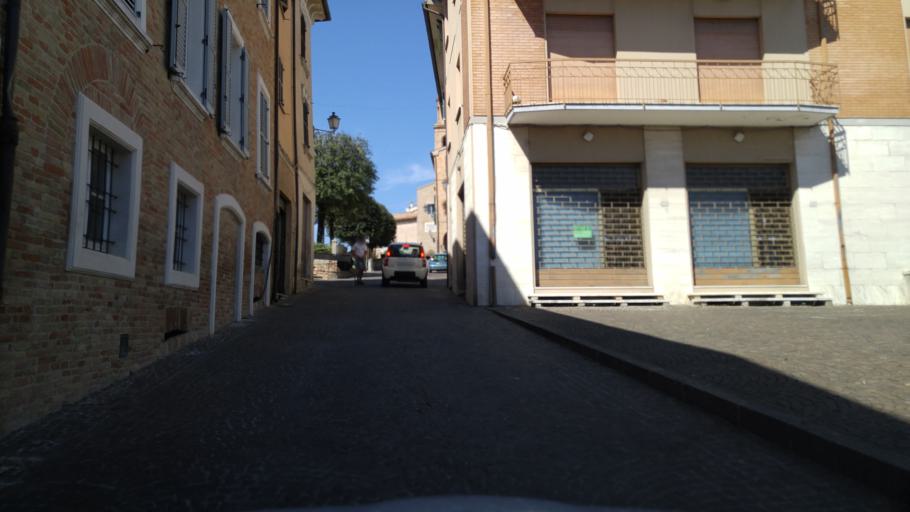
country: IT
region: The Marches
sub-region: Provincia di Pesaro e Urbino
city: Orciano di Pesaro
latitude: 43.6879
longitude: 12.9648
